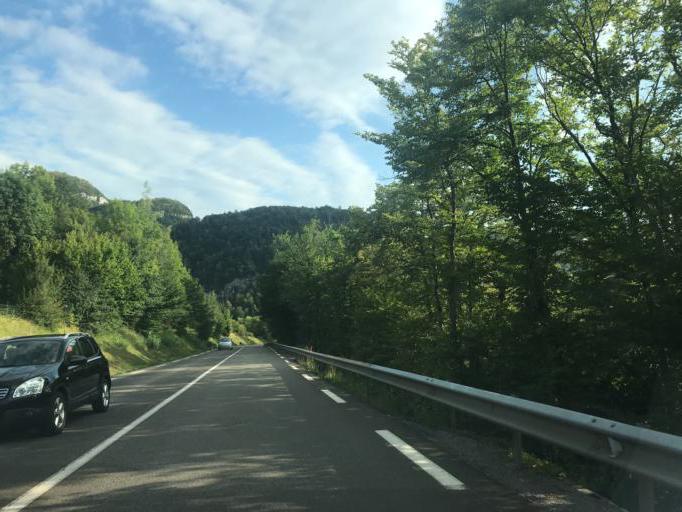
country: FR
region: Franche-Comte
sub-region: Departement du Jura
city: Saint-Lupicin
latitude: 46.3869
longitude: 5.8031
